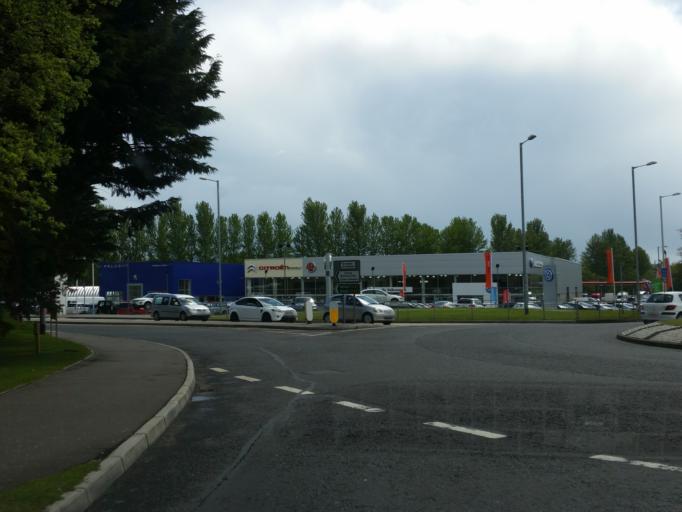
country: GB
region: Northern Ireland
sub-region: Fermanagh District
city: Enniskillen
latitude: 54.3609
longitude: -7.6344
